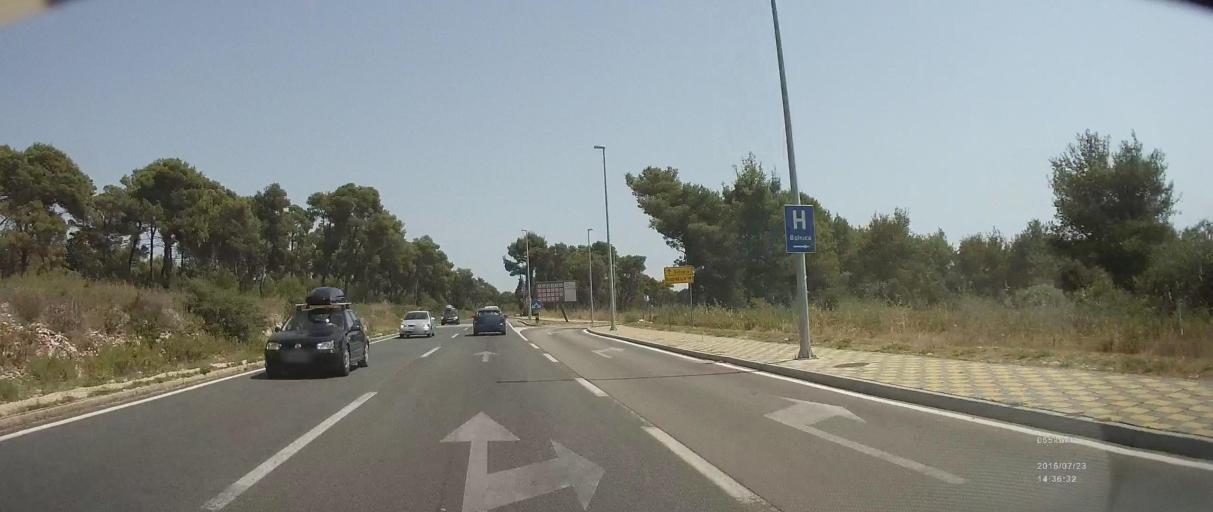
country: HR
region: Zadarska
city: Biograd na Moru
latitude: 43.9514
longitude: 15.4467
